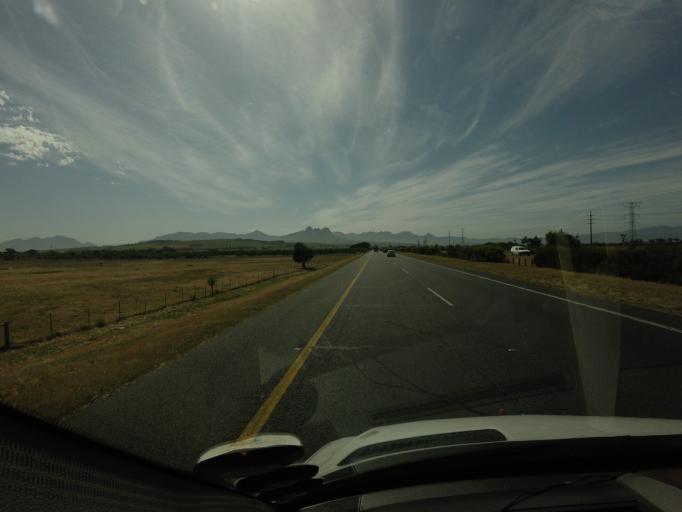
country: ZA
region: Western Cape
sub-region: Cape Winelands District Municipality
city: Stellenbosch
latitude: -34.0433
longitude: 18.7387
